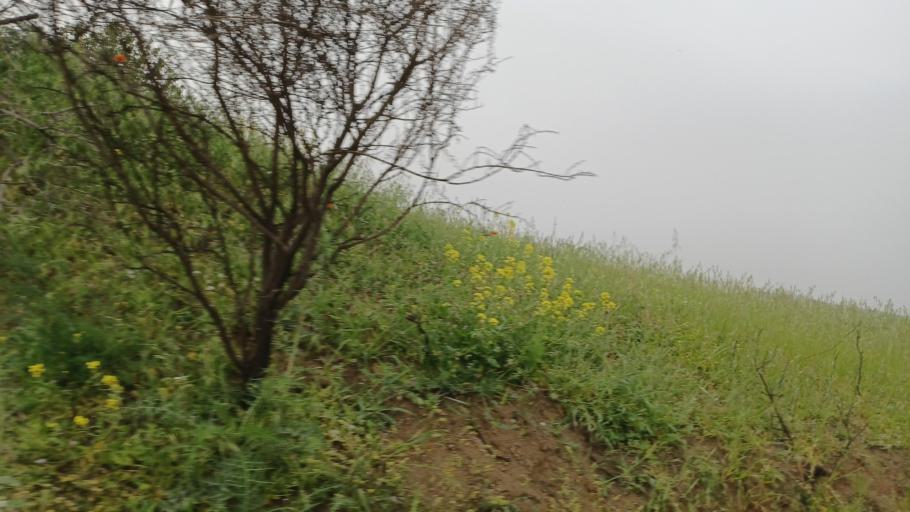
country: CY
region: Limassol
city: Parekklisha
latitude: 34.8513
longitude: 33.1407
